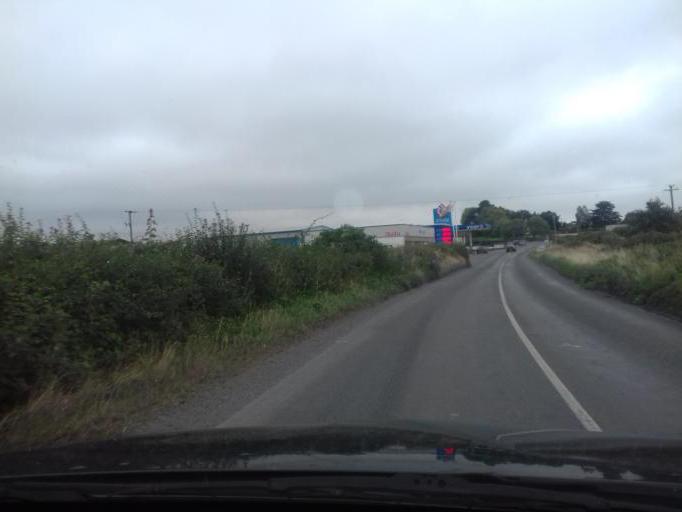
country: IE
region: Leinster
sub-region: County Carlow
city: Bagenalstown
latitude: 52.6875
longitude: -6.9640
